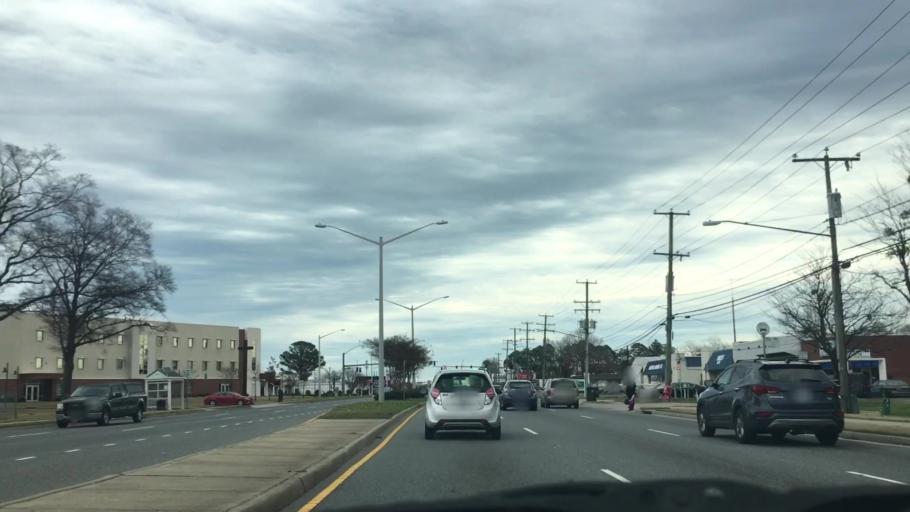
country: US
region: Virginia
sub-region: City of Norfolk
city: Norfolk
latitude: 36.8564
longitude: -76.2251
